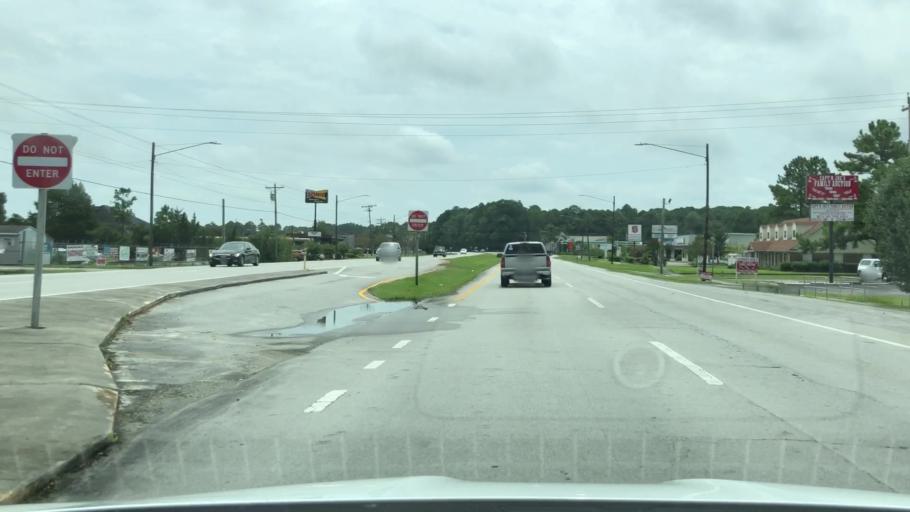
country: US
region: North Carolina
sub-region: Craven County
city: Havelock
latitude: 34.8605
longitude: -76.8974
